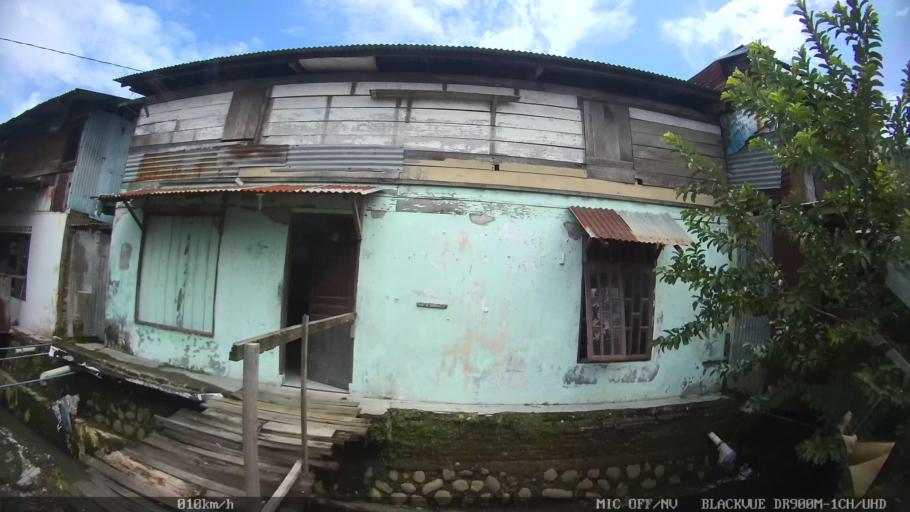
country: ID
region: North Sumatra
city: Medan
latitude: 3.5919
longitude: 98.7401
